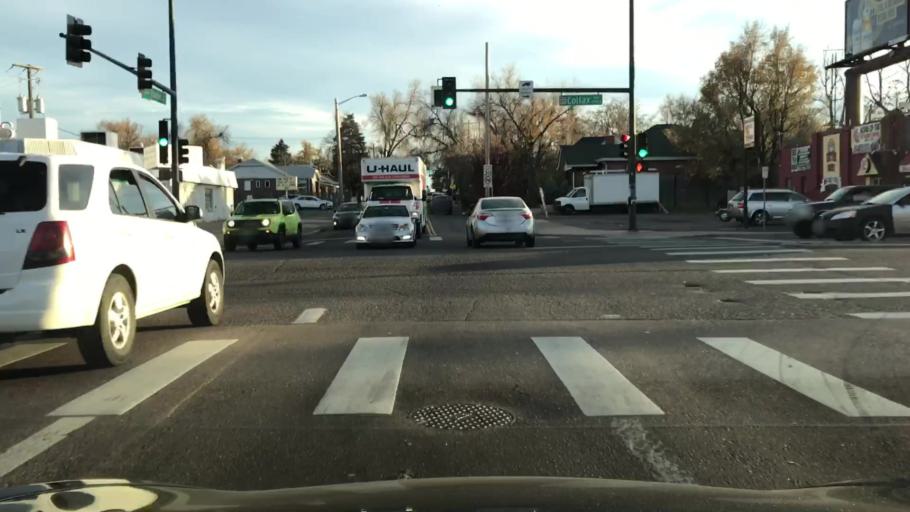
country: US
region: Colorado
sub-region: Arapahoe County
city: Glendale
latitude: 39.7404
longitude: -104.9035
